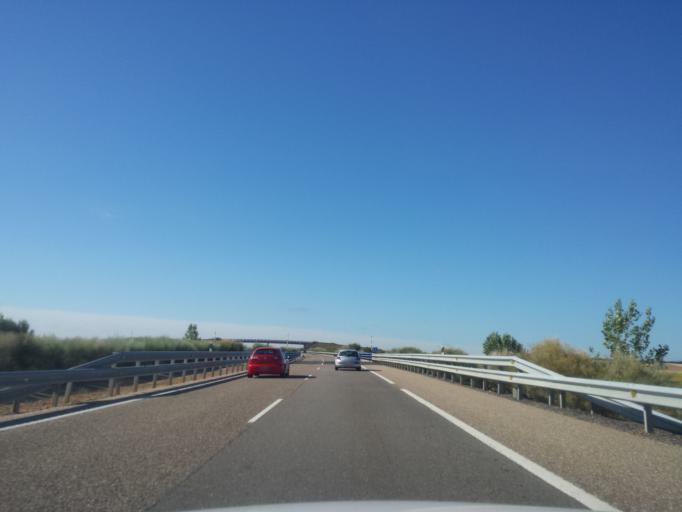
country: ES
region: Castille and Leon
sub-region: Provincia de Zamora
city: Matilla de Arzon
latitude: 42.1114
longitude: -5.6595
